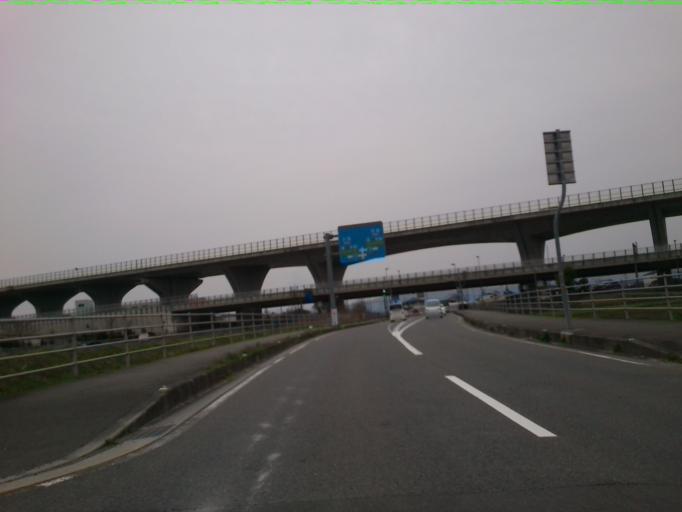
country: JP
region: Kyoto
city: Yawata
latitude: 34.8498
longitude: 135.7322
